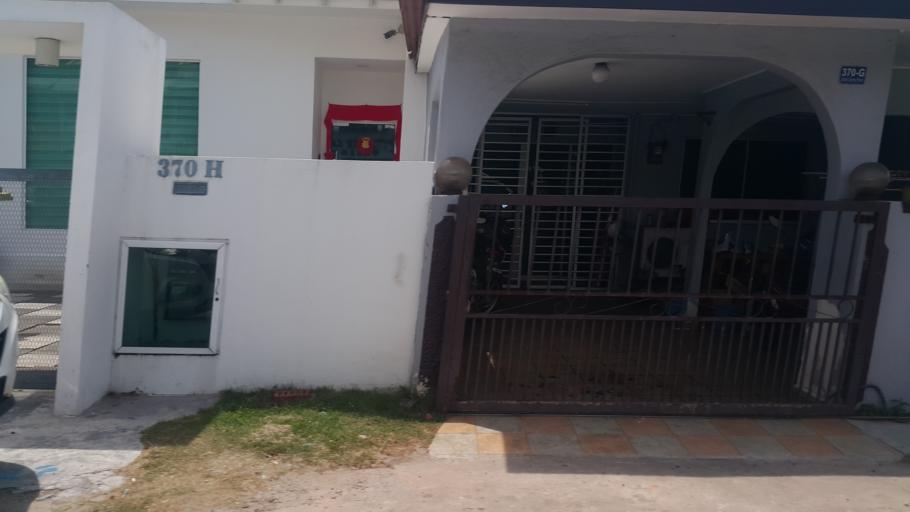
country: MY
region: Melaka
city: Kampung Bukit Baharu
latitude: 2.1866
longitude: 102.2736
